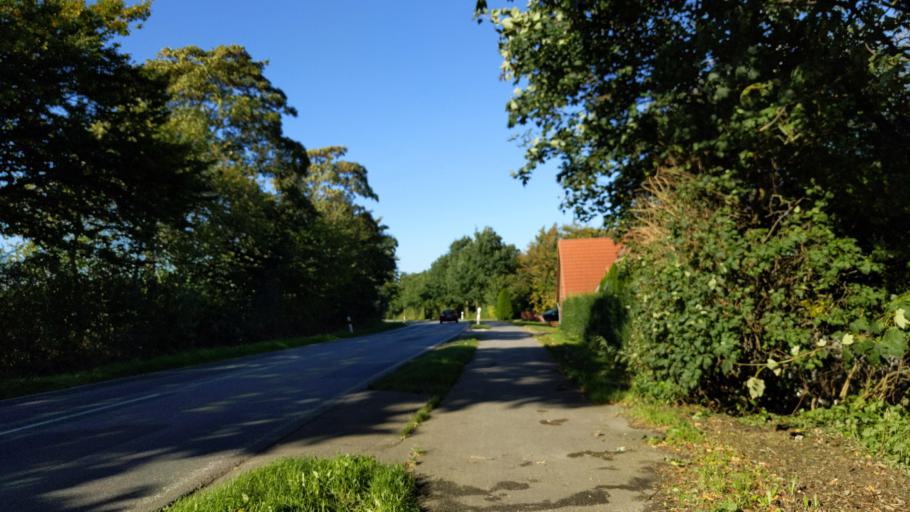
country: DE
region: Schleswig-Holstein
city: Ahrensbok
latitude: 53.9950
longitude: 10.5783
